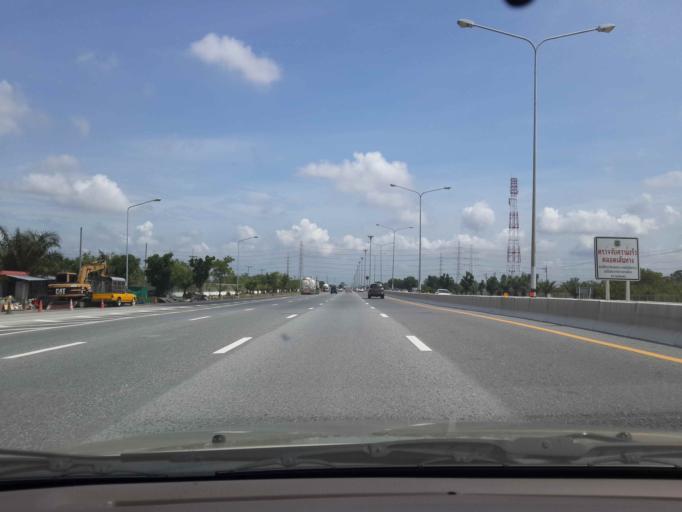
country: TH
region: Chachoengsao
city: Bang Pakong
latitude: 13.5046
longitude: 101.0380
